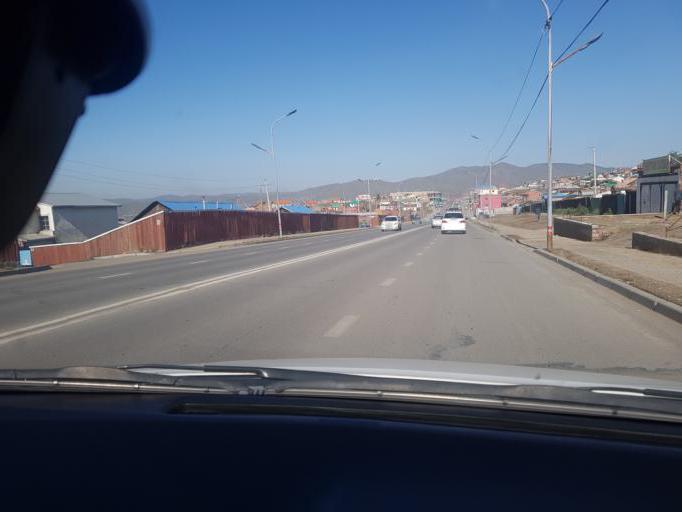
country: MN
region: Ulaanbaatar
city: Ulaanbaatar
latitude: 47.9518
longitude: 106.8573
